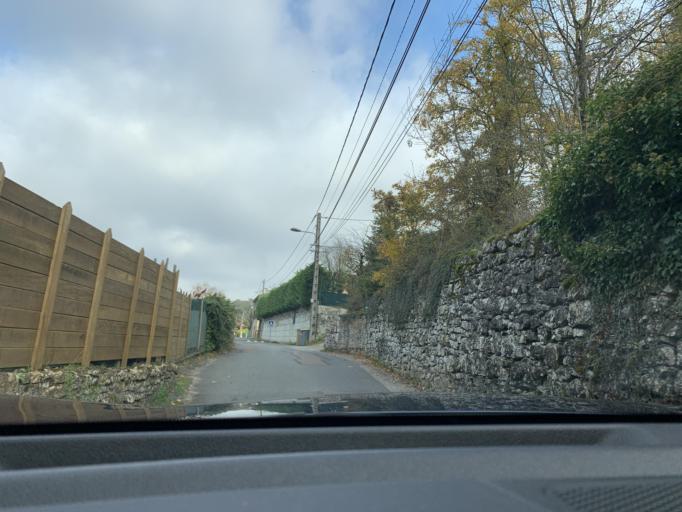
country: FR
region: Rhone-Alpes
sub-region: Departement du Rhone
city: Charnay
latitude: 45.8749
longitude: 4.6483
